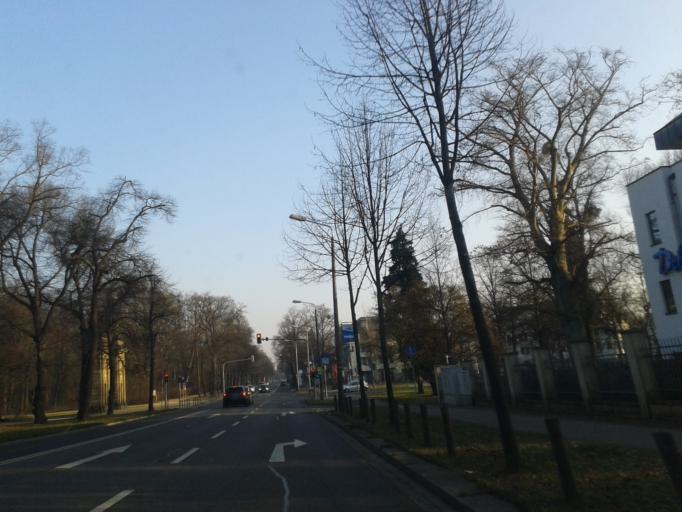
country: DE
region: Saxony
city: Dresden
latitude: 51.0325
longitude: 13.7739
